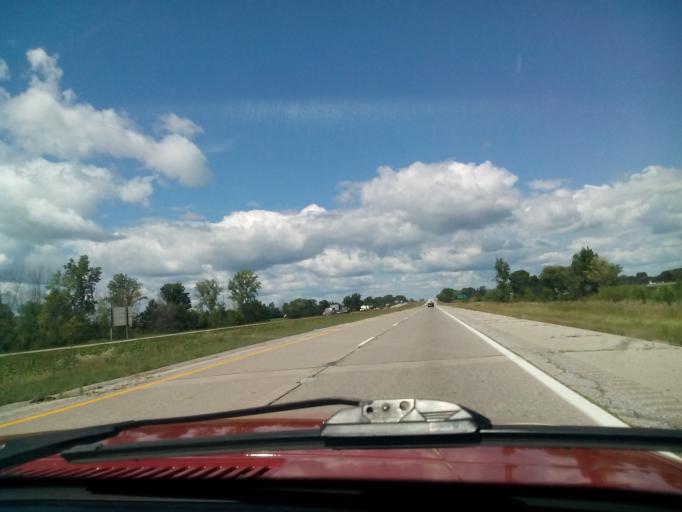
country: US
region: Michigan
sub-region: Bay County
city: Bay City
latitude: 43.6316
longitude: -83.9638
